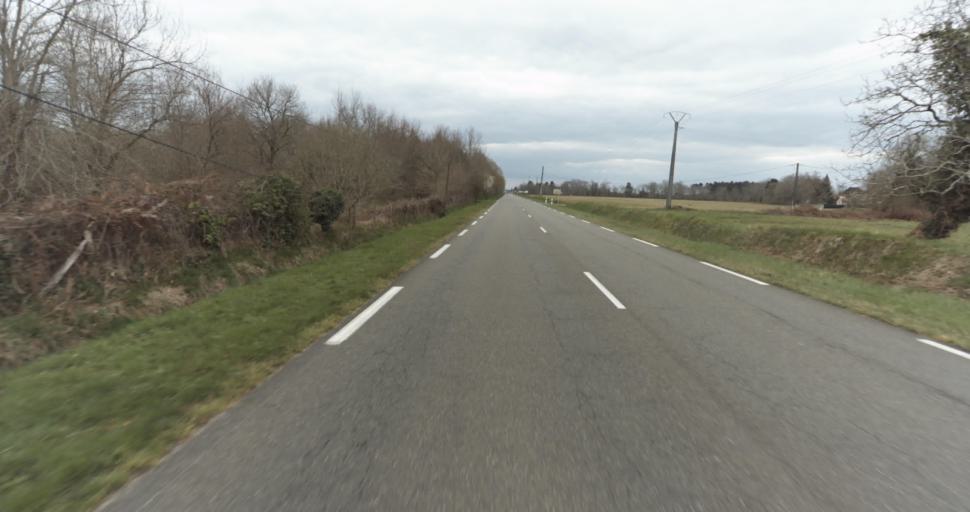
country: FR
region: Aquitaine
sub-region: Departement des Landes
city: Sarbazan
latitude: 44.0135
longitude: -0.3245
